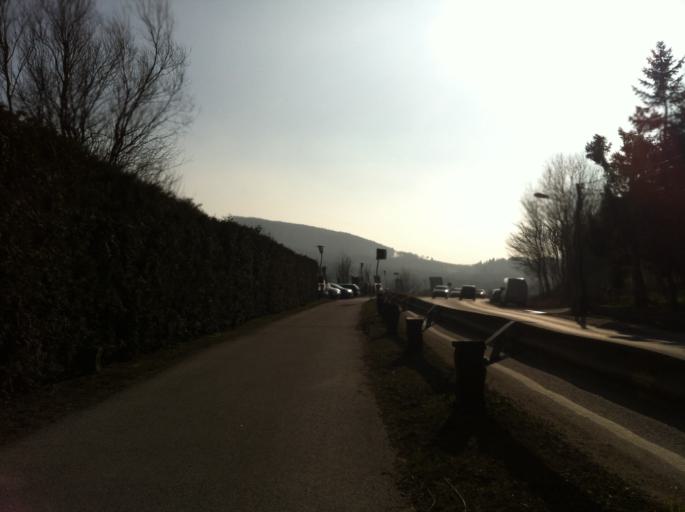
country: AT
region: Lower Austria
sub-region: Politischer Bezirk Wien-Umgebung
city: Wolfsgraben
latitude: 48.1839
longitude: 16.1219
